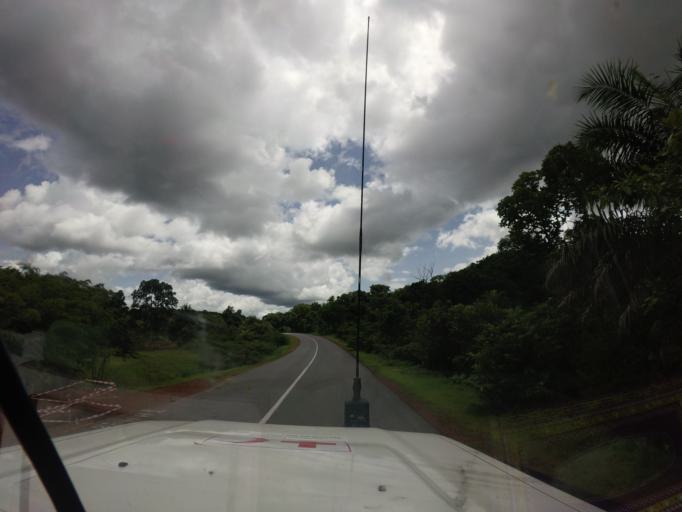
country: SL
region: Northern Province
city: Bindi
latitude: 10.1612
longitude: -11.5215
